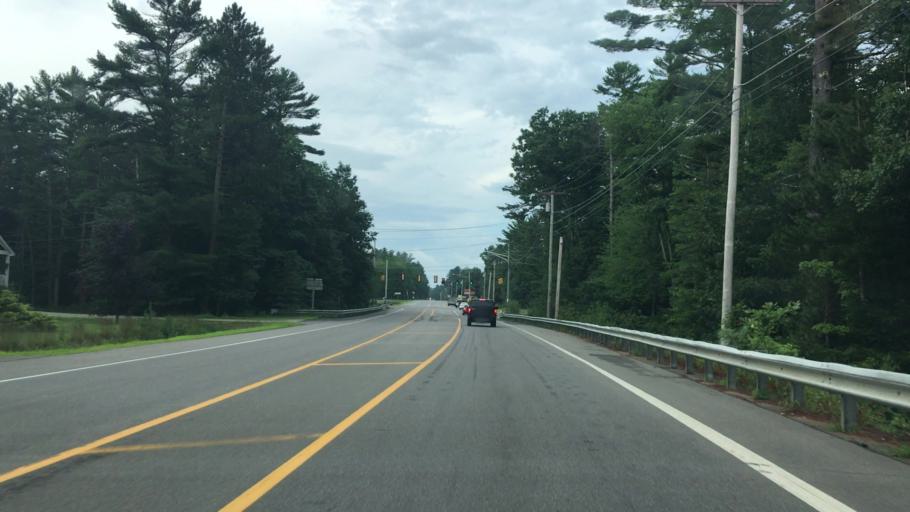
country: US
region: New Hampshire
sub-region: Strafford County
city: Rochester
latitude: 43.3521
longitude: -70.9269
